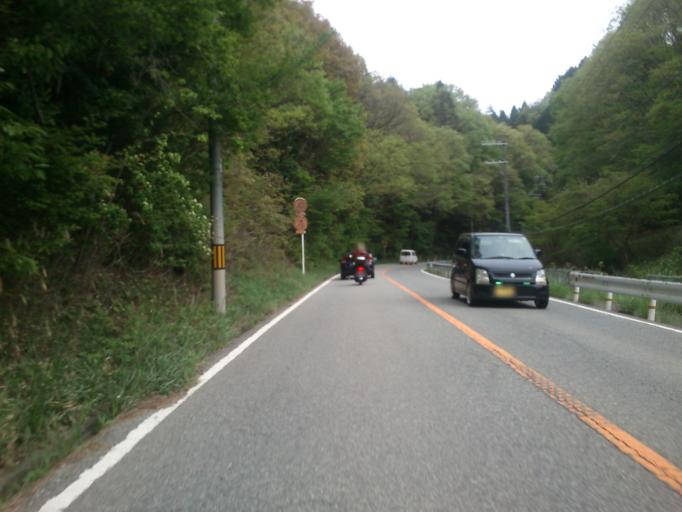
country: JP
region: Kyoto
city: Kameoka
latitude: 34.9601
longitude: 135.5113
